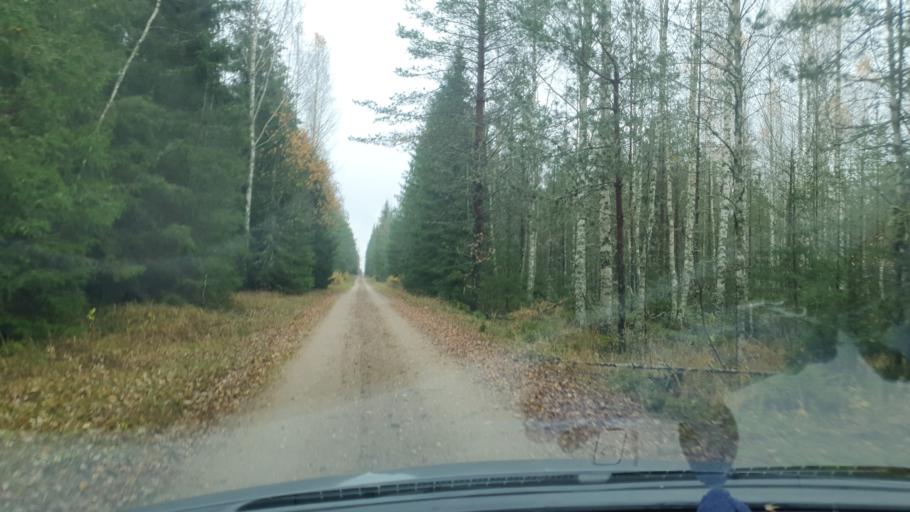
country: EE
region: Viljandimaa
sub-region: Karksi vald
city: Karksi-Nuia
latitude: 57.9734
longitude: 25.6149
